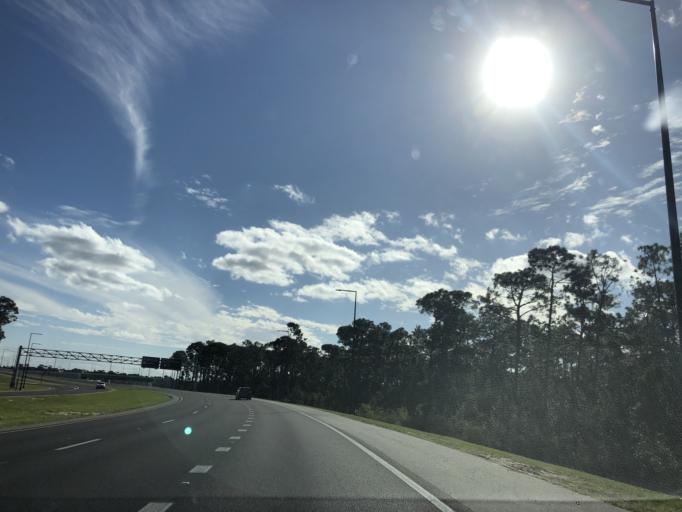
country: US
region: Florida
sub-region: Osceola County
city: Celebration
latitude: 28.3536
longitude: -81.5534
